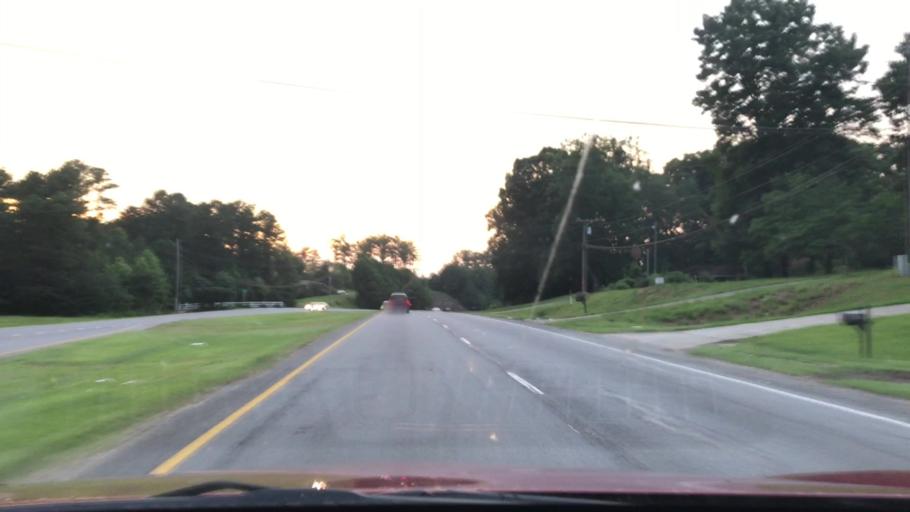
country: US
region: Georgia
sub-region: Gwinnett County
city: Lawrenceville
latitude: 33.9945
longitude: -83.9881
